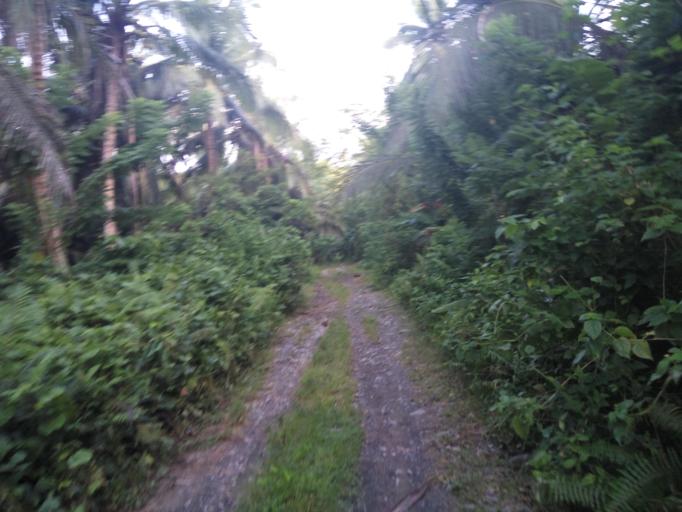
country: PH
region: Central Luzon
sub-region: Province of Aurora
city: Maria Aurora
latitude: 15.8889
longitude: 121.5471
